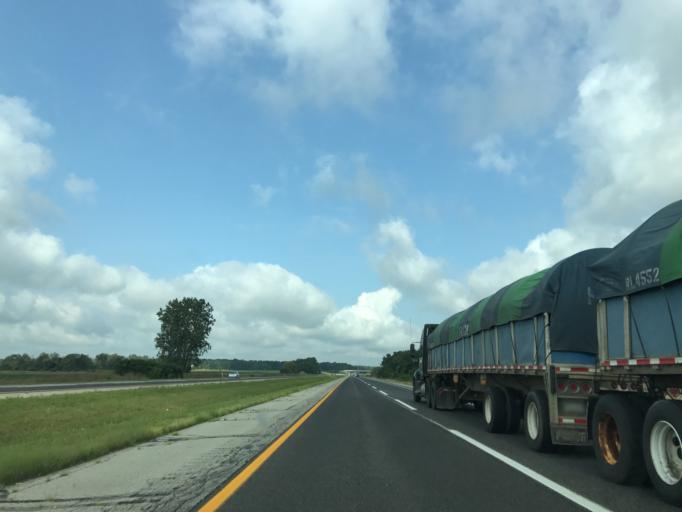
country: US
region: Indiana
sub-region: Steuben County
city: Fremont
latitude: 41.6886
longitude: -84.8921
